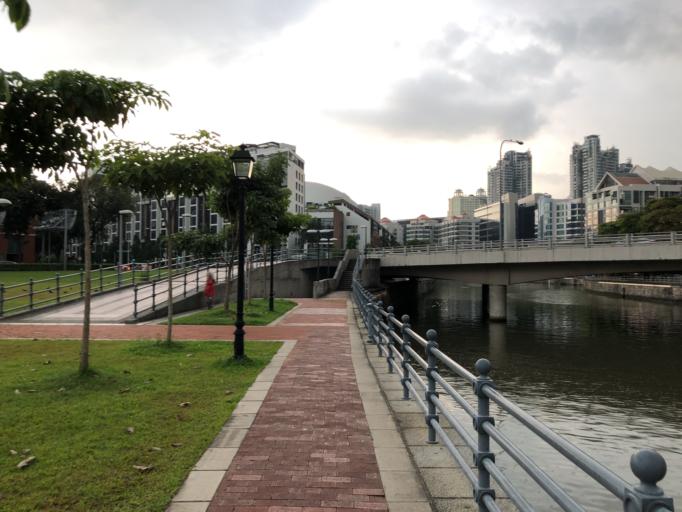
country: SG
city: Singapore
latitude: 1.2906
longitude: 103.8431
